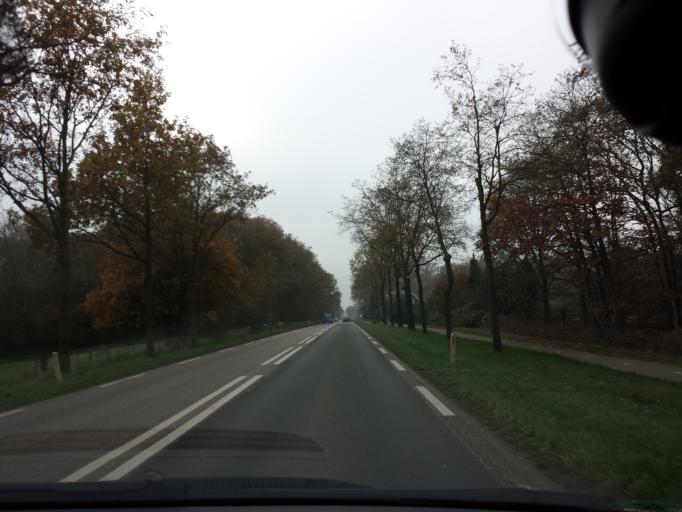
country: NL
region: Limburg
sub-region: Gemeente Beesel
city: Beesel
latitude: 51.2776
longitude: 6.0128
